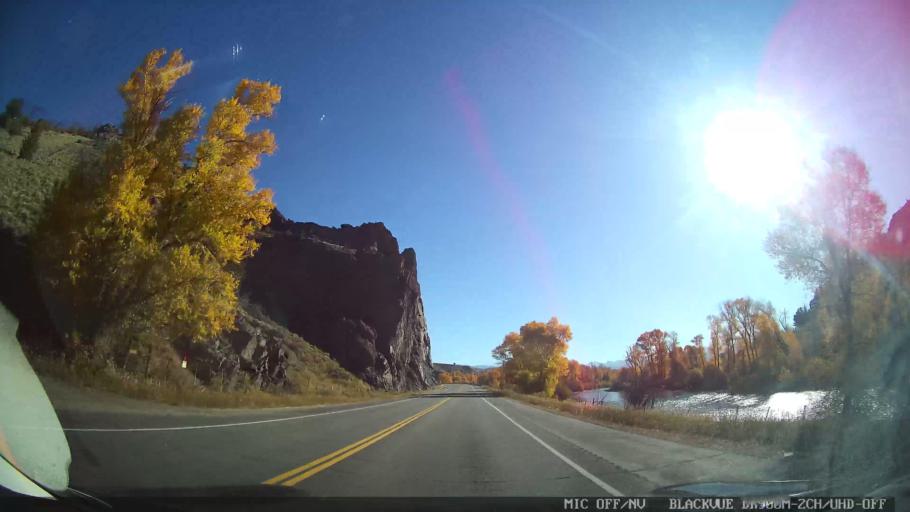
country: US
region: Colorado
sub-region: Grand County
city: Granby
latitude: 40.1090
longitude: -106.0030
